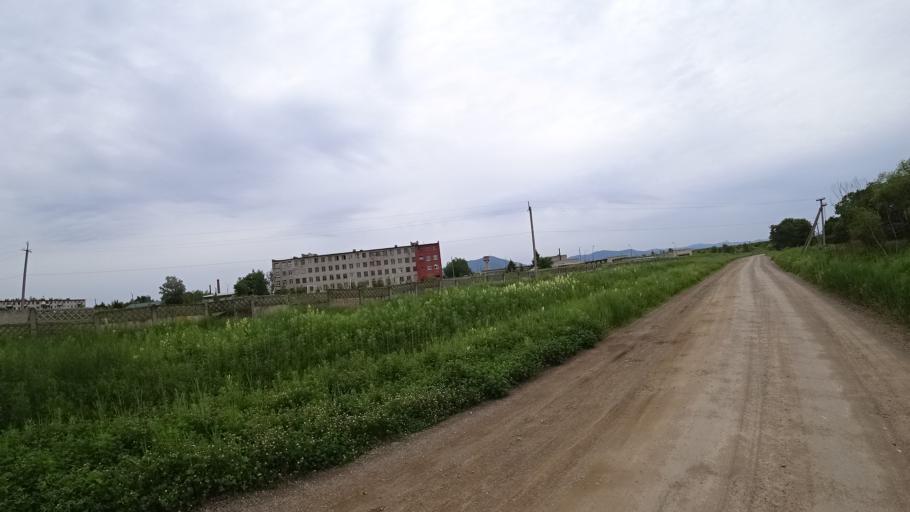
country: RU
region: Primorskiy
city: Arsen'yev
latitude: 44.2013
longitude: 133.3110
